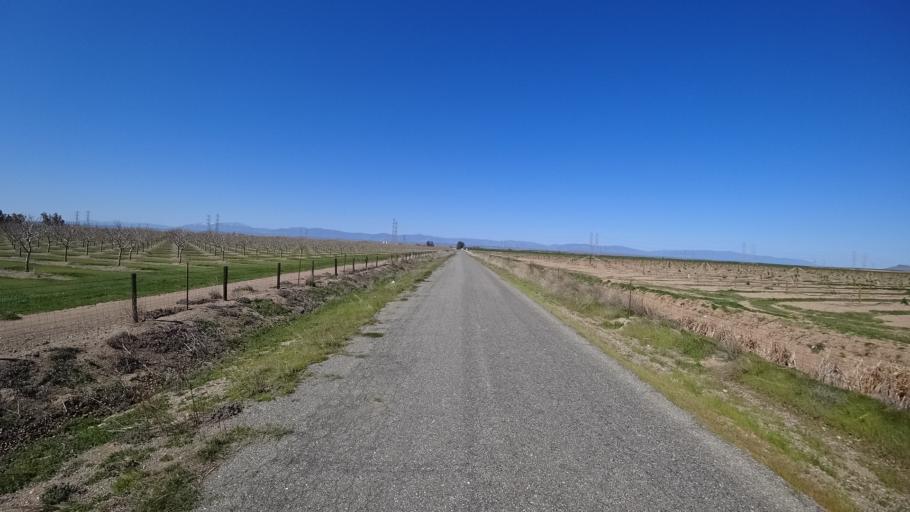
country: US
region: California
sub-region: Glenn County
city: Orland
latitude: 39.6538
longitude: -122.2596
